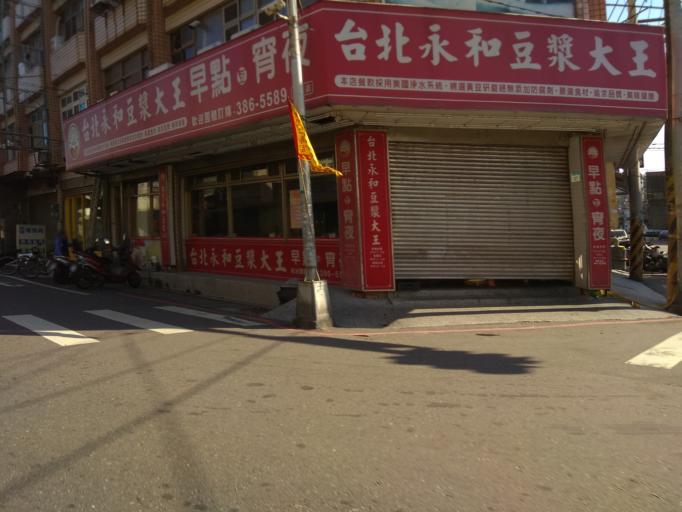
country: TW
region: Taiwan
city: Taoyuan City
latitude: 25.0651
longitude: 121.1942
